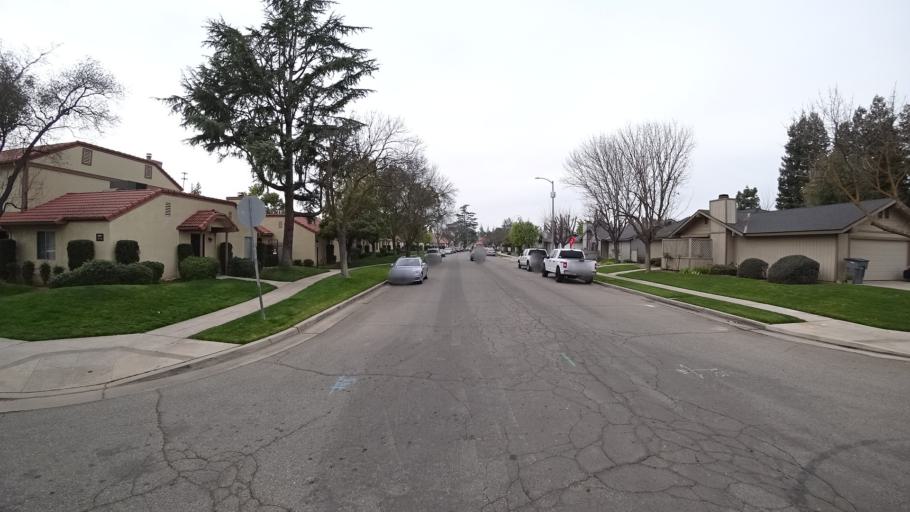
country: US
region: California
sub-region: Fresno County
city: Clovis
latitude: 36.8540
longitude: -119.7965
